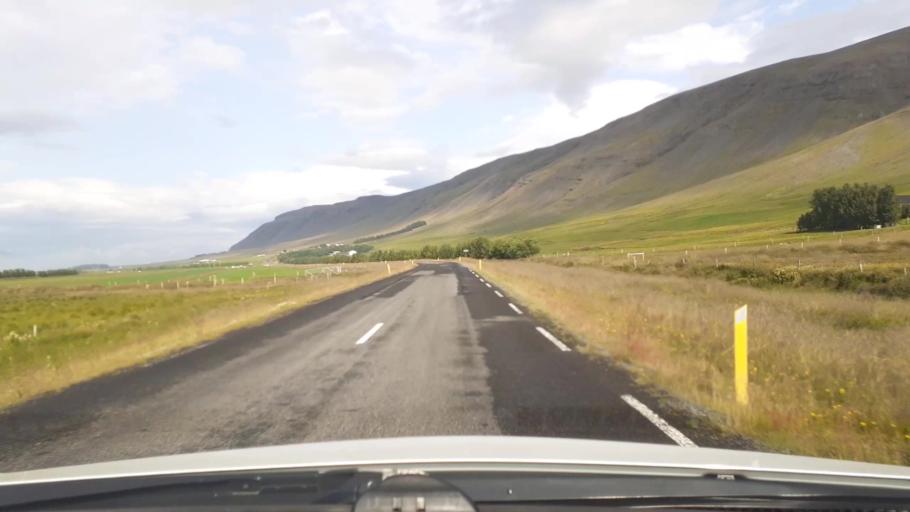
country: IS
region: Capital Region
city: Mosfellsbaer
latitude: 64.3366
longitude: -21.5289
